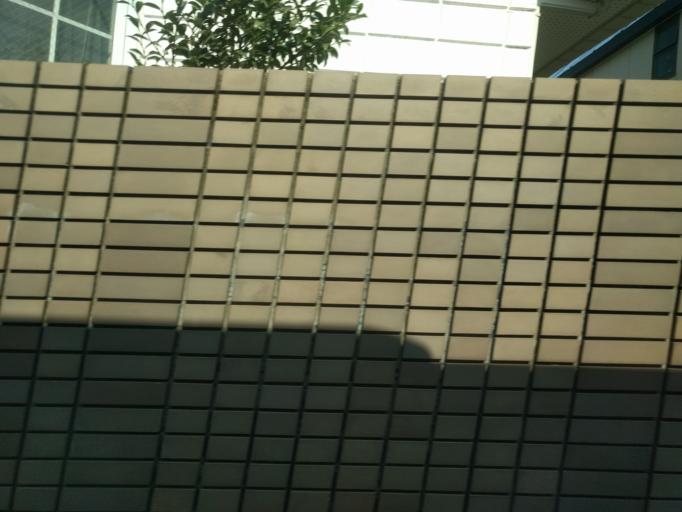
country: JP
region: Tokyo
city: Tokyo
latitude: 35.6208
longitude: 139.6472
